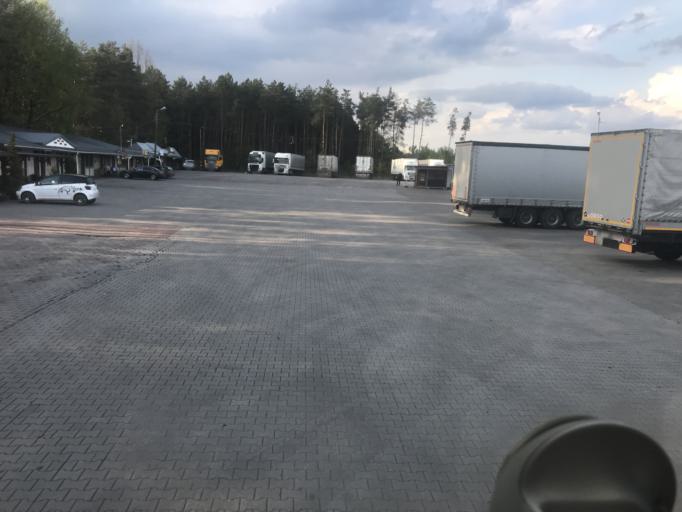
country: PL
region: Masovian Voivodeship
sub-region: Powiat otwocki
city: Kolbiel
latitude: 52.1227
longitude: 21.4983
